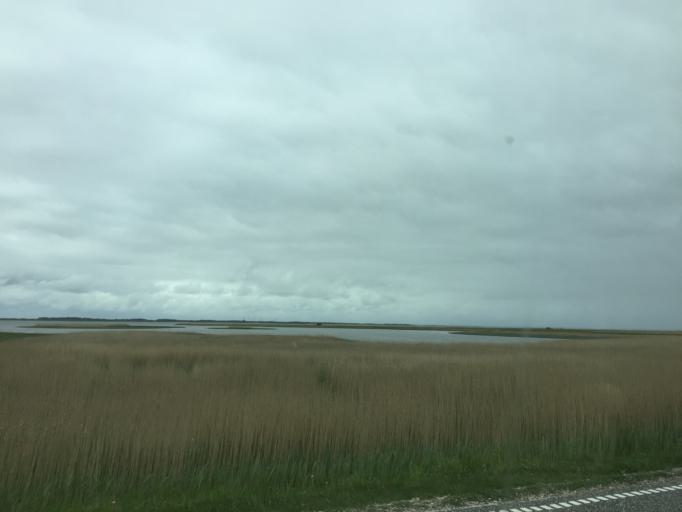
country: DK
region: Central Jutland
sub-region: Lemvig Kommune
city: Harboore
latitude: 56.4006
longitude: 8.1218
